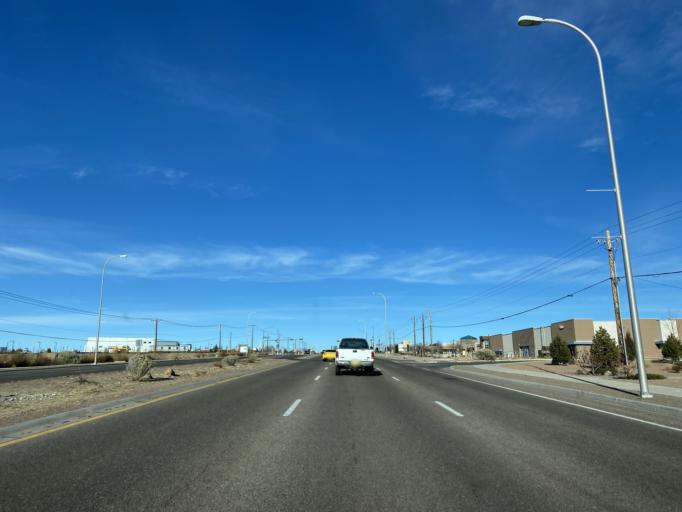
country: US
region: New Mexico
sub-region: Santa Fe County
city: Agua Fria
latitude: 35.6182
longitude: -106.0300
